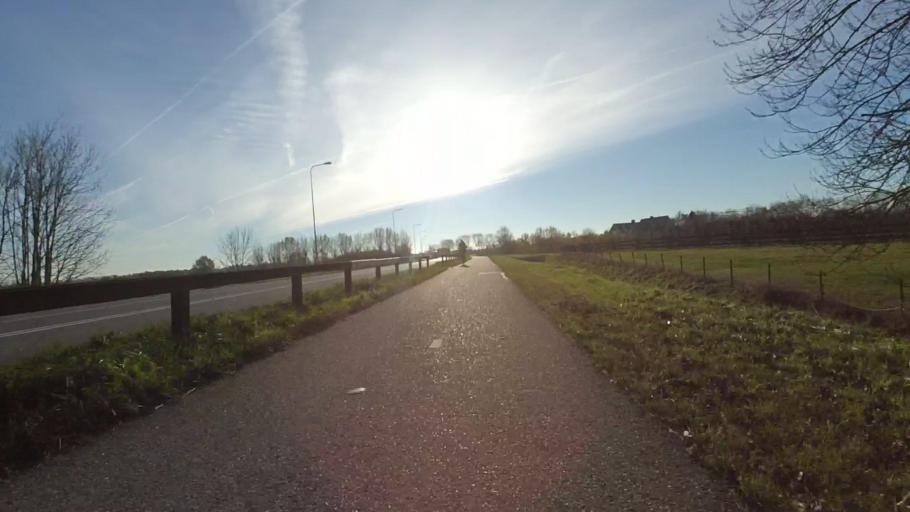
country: NL
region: Utrecht
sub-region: Gemeente Wijk bij Duurstede
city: Wijk bij Duurstede
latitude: 51.9927
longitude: 5.3254
